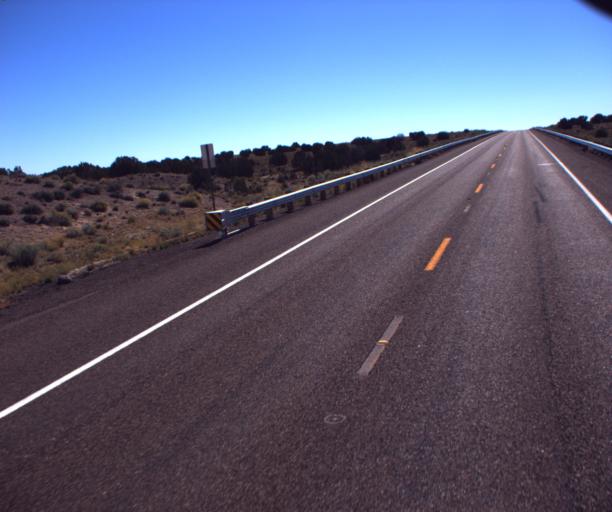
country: US
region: Arizona
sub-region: Apache County
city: Saint Johns
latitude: 34.6605
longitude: -109.7151
